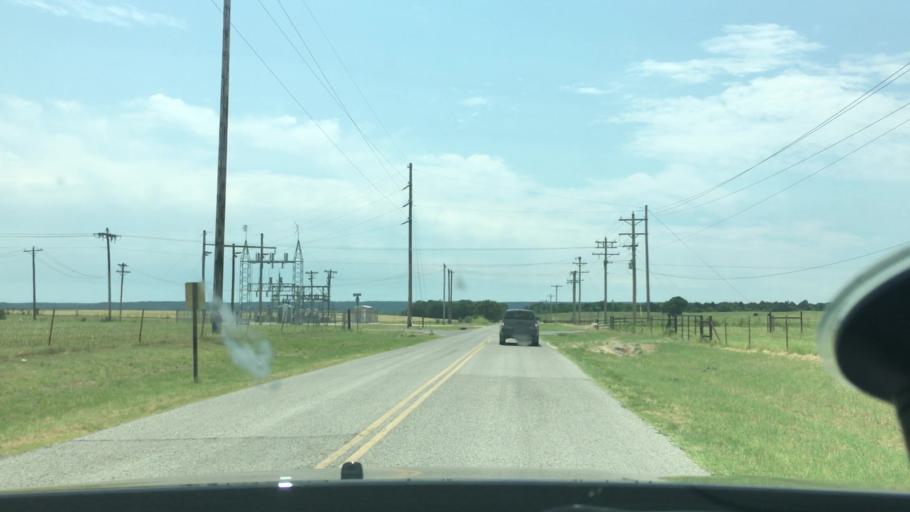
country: US
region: Oklahoma
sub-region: Love County
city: Marietta
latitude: 33.9120
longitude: -97.3521
